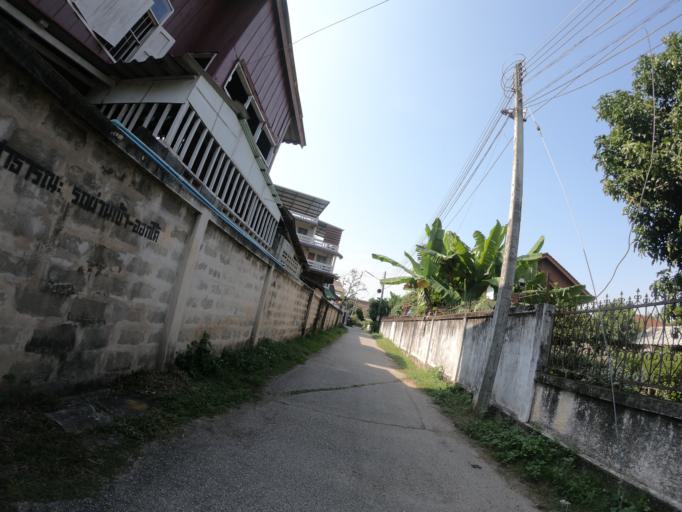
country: TH
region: Chiang Mai
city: Chiang Mai
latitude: 18.7966
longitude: 99.0180
